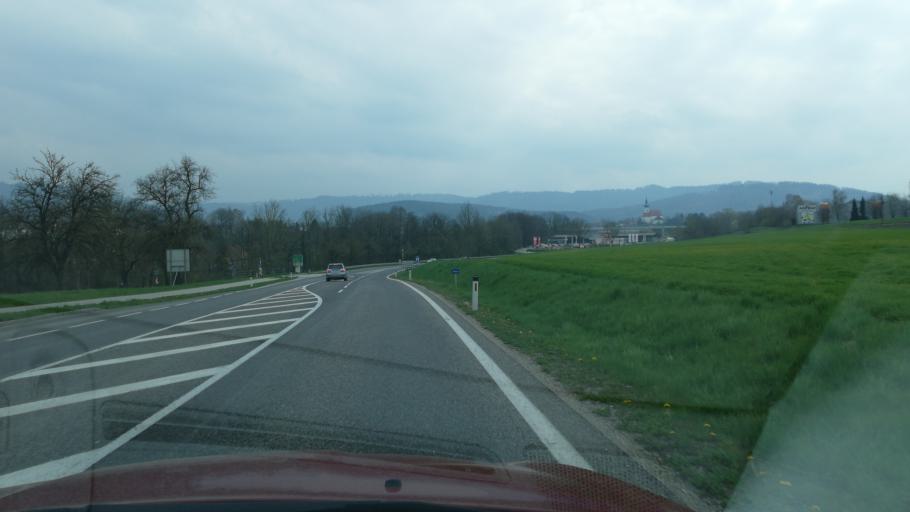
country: AT
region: Upper Austria
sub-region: Politischer Bezirk Vocklabruck
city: Lenzing
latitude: 47.9589
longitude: 13.6066
